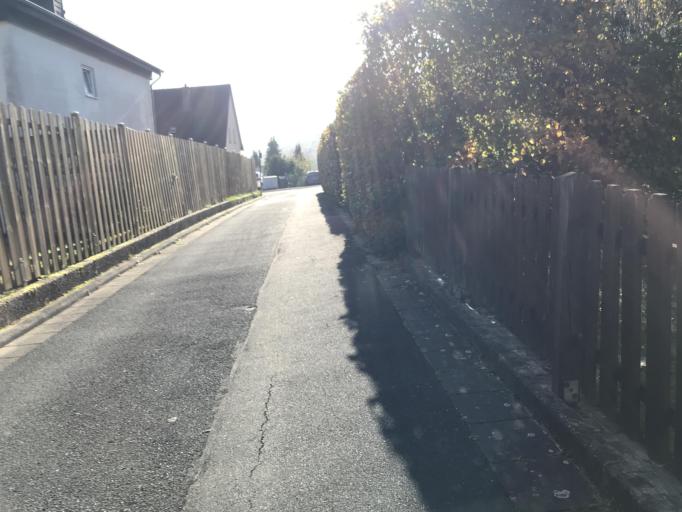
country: DE
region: Hesse
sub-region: Regierungsbezirk Giessen
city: Braunfels
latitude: 50.5162
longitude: 8.4017
